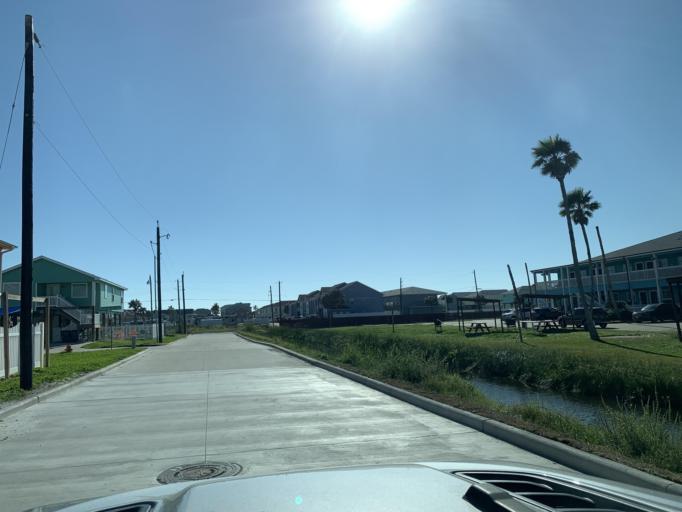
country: US
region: Texas
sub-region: Nueces County
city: Port Aransas
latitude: 27.8186
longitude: -97.0731
